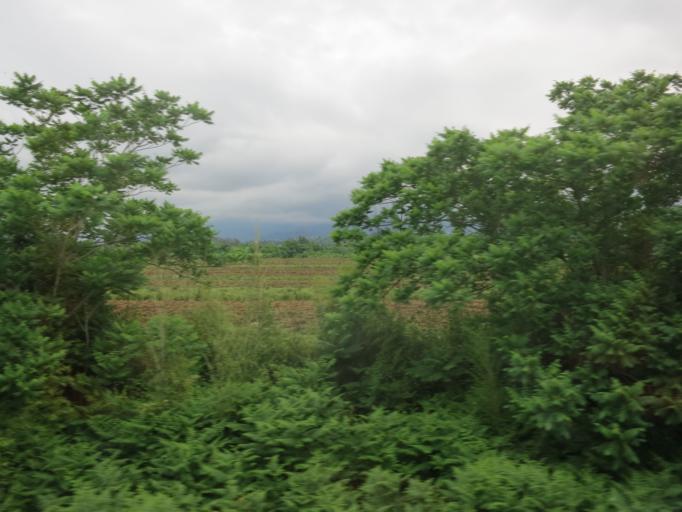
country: GE
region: Ajaria
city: Kobuleti
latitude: 41.7971
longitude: 41.7725
